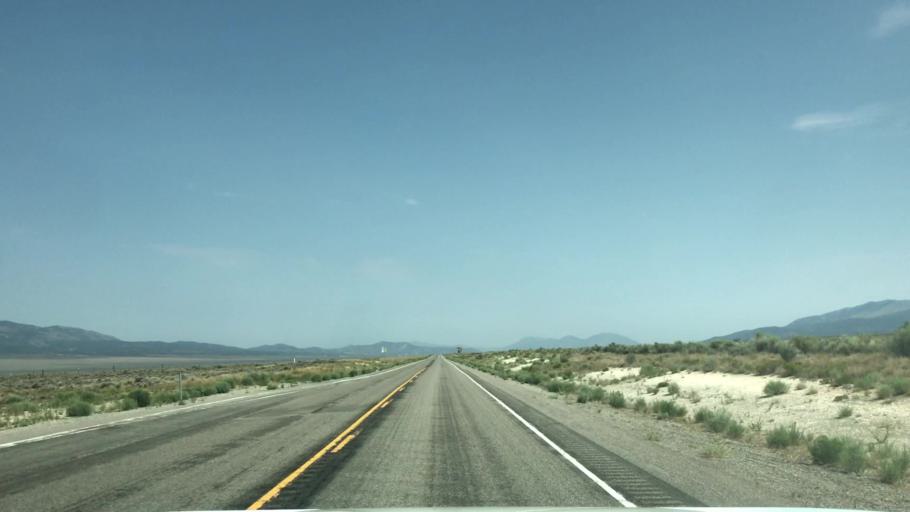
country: US
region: Nevada
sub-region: White Pine County
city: Ely
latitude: 39.0493
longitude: -114.7240
